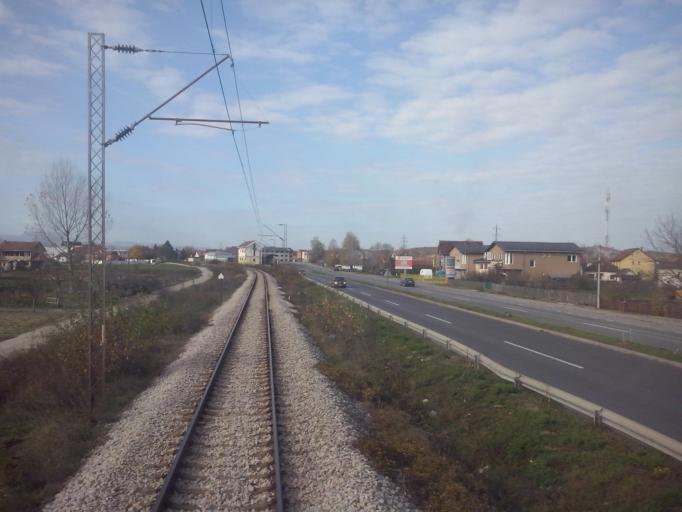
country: RS
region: Central Serbia
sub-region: Kolubarski Okrug
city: Valjevo
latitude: 44.2935
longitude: 19.9666
